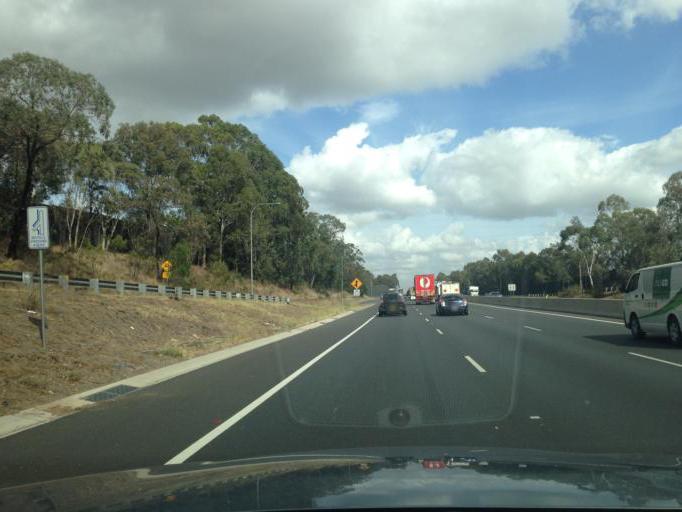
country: AU
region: New South Wales
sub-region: Bankstown
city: Revesby
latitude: -33.9408
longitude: 151.0171
